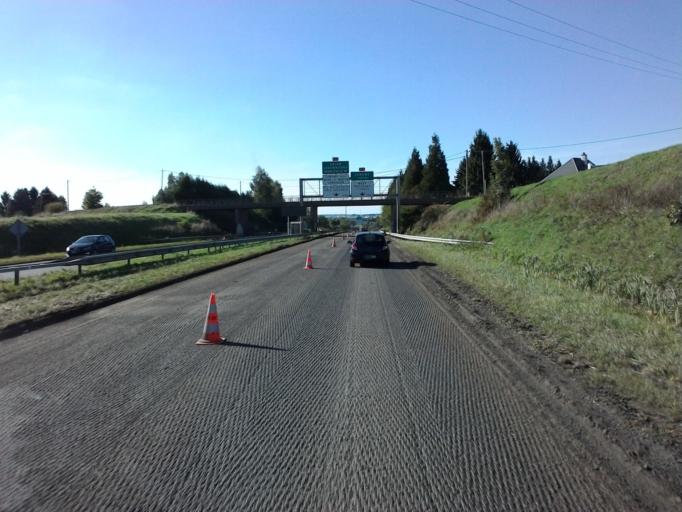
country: FR
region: Lorraine
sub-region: Departement de Meurthe-et-Moselle
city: Haucourt-Moulaine
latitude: 49.5014
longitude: 5.7964
